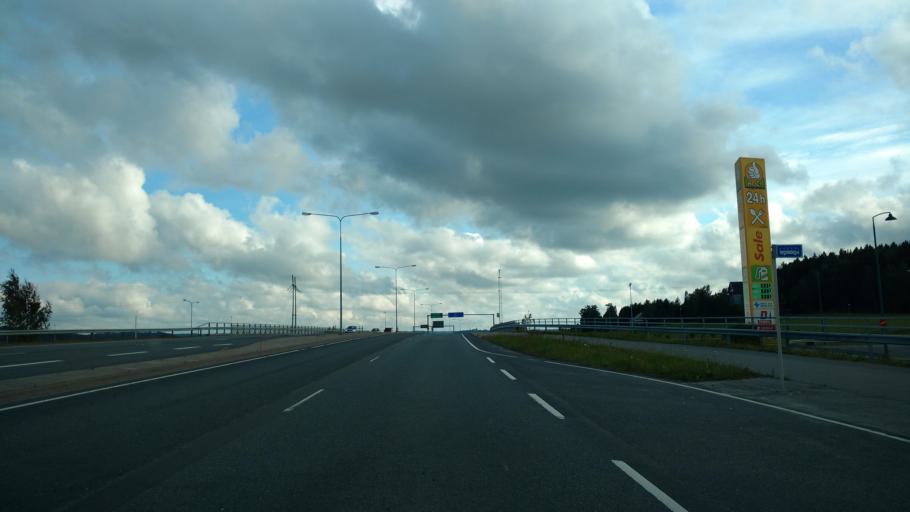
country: FI
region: Varsinais-Suomi
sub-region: Salo
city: Salo
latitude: 60.4188
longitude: 23.1661
